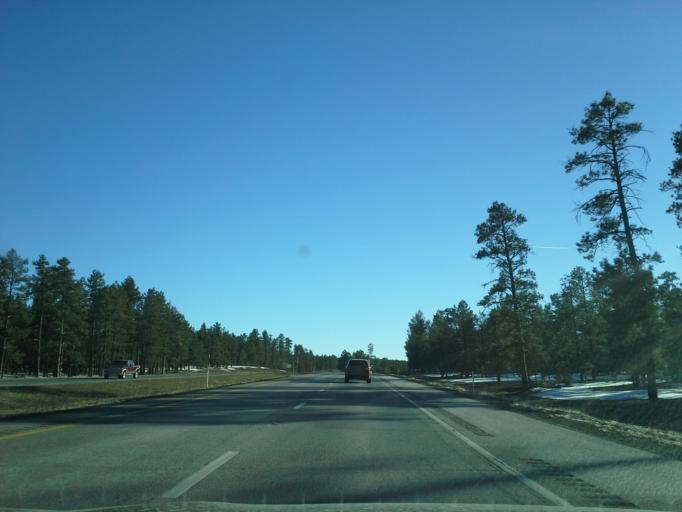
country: US
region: Arizona
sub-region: Coconino County
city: Sedona
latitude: 34.8403
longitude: -111.6043
